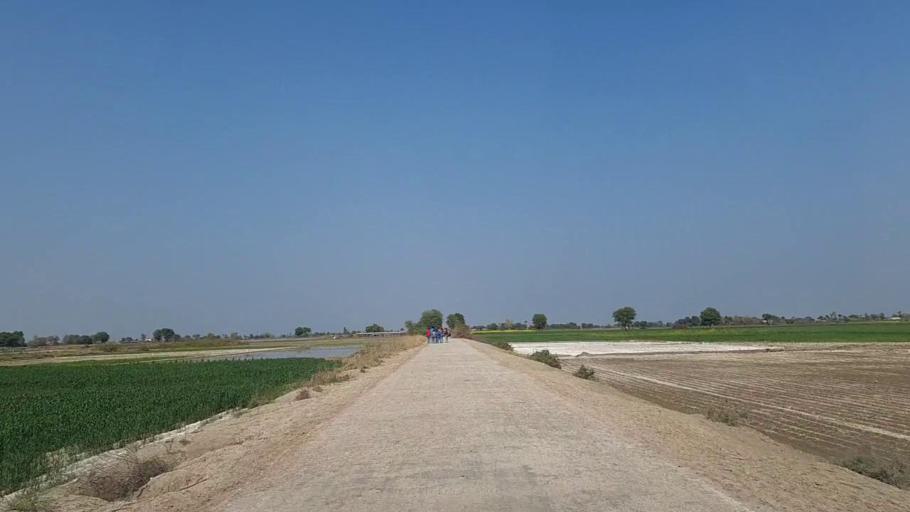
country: PK
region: Sindh
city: Nawabshah
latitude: 26.2682
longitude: 68.5133
